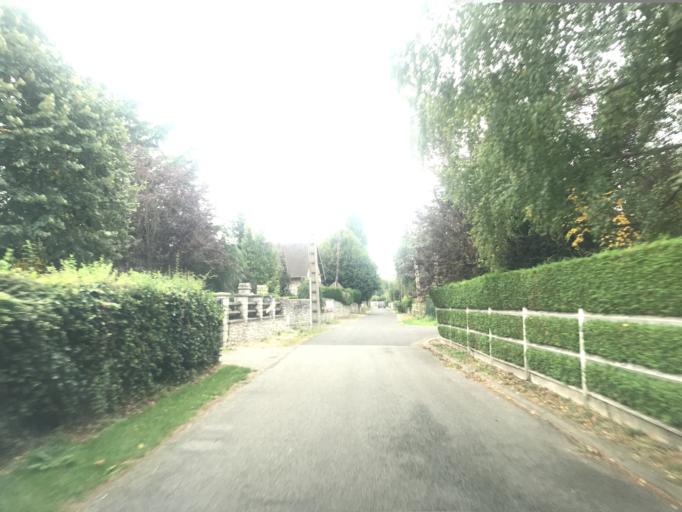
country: FR
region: Haute-Normandie
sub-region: Departement de l'Eure
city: Houlbec-Cocherel
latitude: 49.0733
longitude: 1.2880
